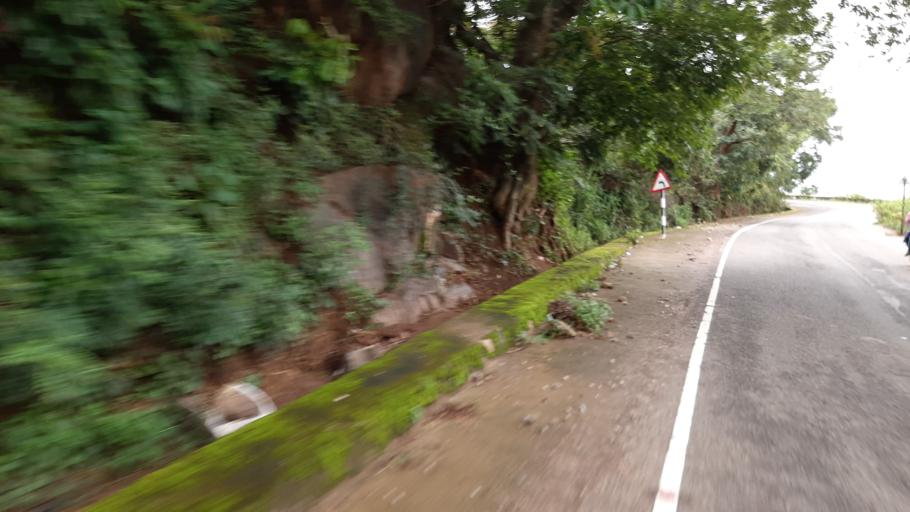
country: IN
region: Andhra Pradesh
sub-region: Vizianagaram District
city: Salur
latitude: 18.2398
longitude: 83.0259
